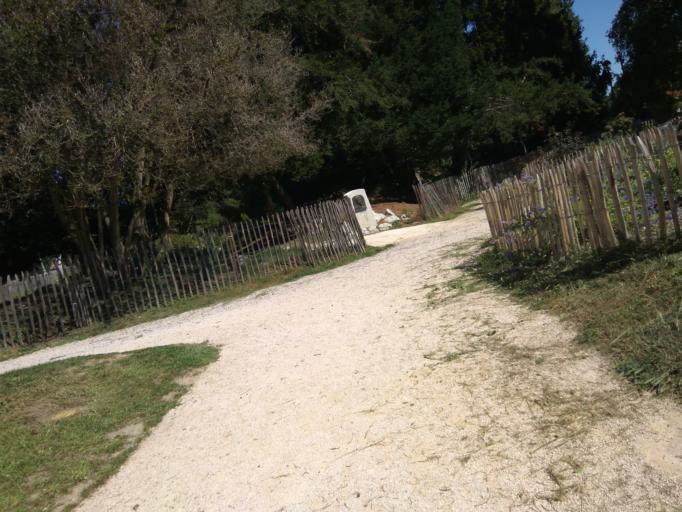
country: FR
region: Aquitaine
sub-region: Departement des Pyrenees-Atlantiques
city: Pau
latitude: 43.2952
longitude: -0.3600
